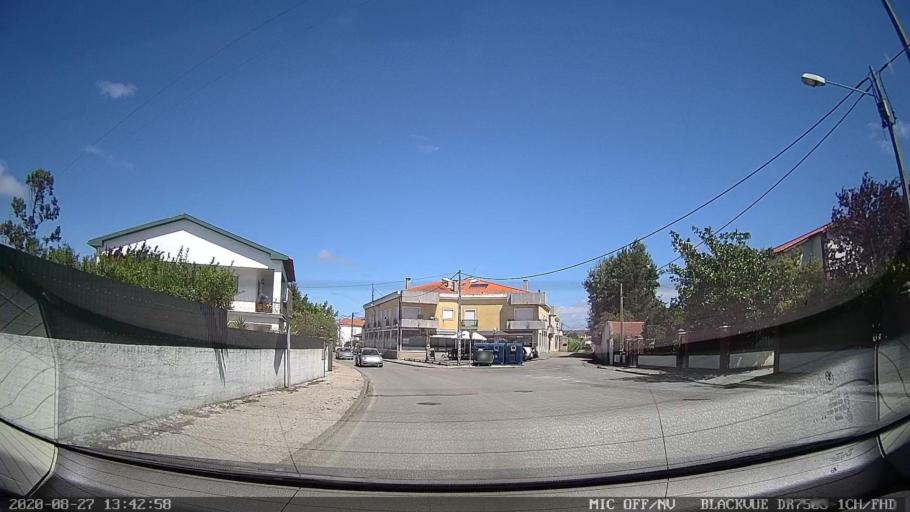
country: PT
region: Coimbra
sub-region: Mira
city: Mira
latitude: 40.4236
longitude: -8.7382
